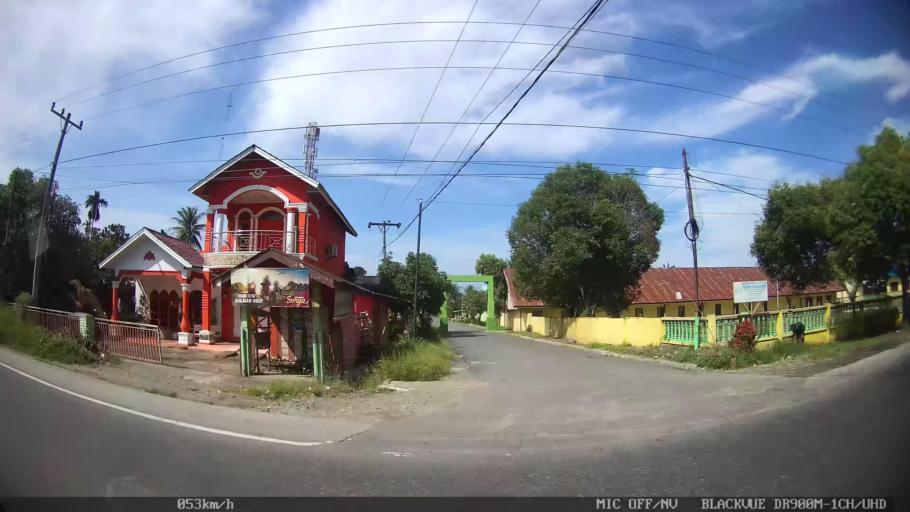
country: ID
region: North Sumatra
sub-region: Kabupaten Langkat
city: Stabat
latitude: 3.7275
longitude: 98.4966
